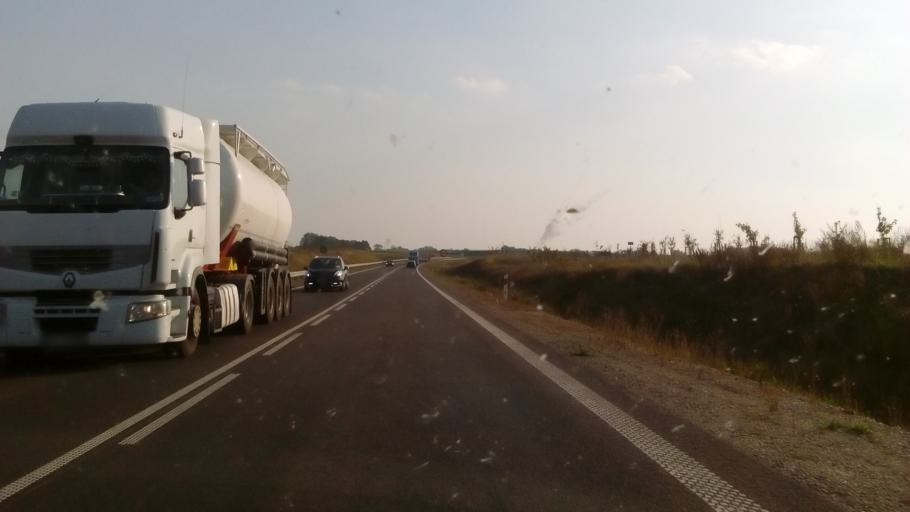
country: PL
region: Podlasie
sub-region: Powiat grajewski
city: Rajgrod
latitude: 53.7722
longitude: 22.8339
